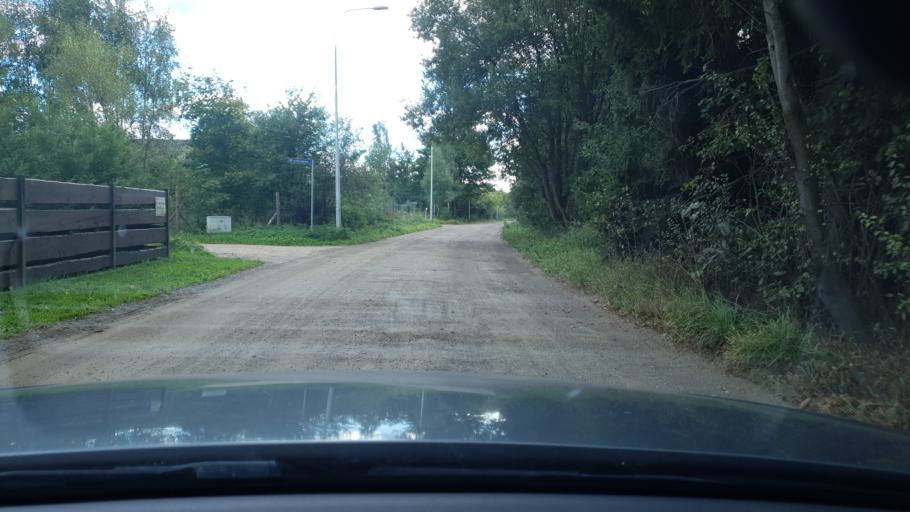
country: PL
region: Pomeranian Voivodeship
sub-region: Powiat wejherowski
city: Reda
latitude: 54.5793
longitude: 18.3121
